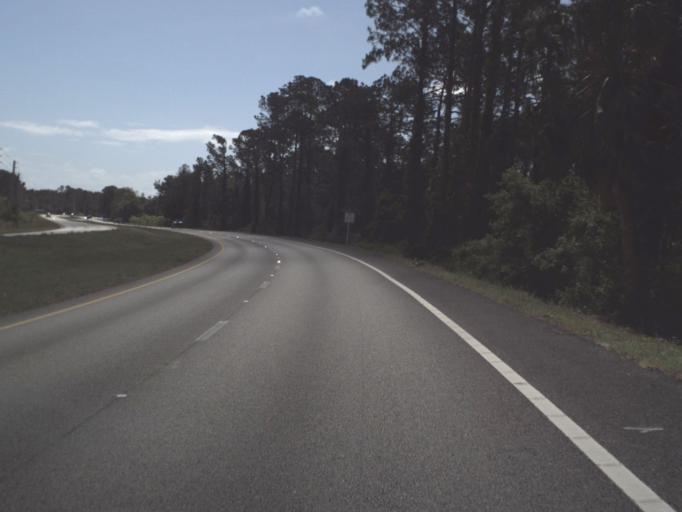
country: US
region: Florida
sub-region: Flagler County
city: Bunnell
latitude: 29.4107
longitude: -81.2036
